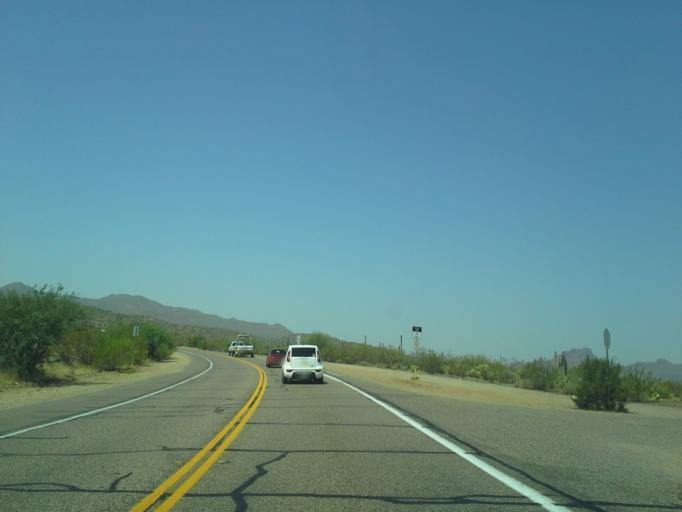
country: US
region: Arizona
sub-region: Pinal County
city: Apache Junction
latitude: 33.5535
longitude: -111.5787
